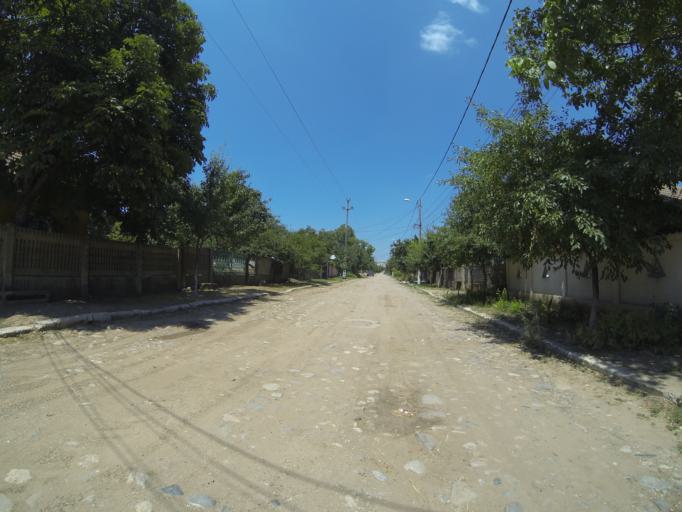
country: RO
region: Dolj
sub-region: Comuna Segarcea
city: Segarcea
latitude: 44.0882
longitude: 23.7459
